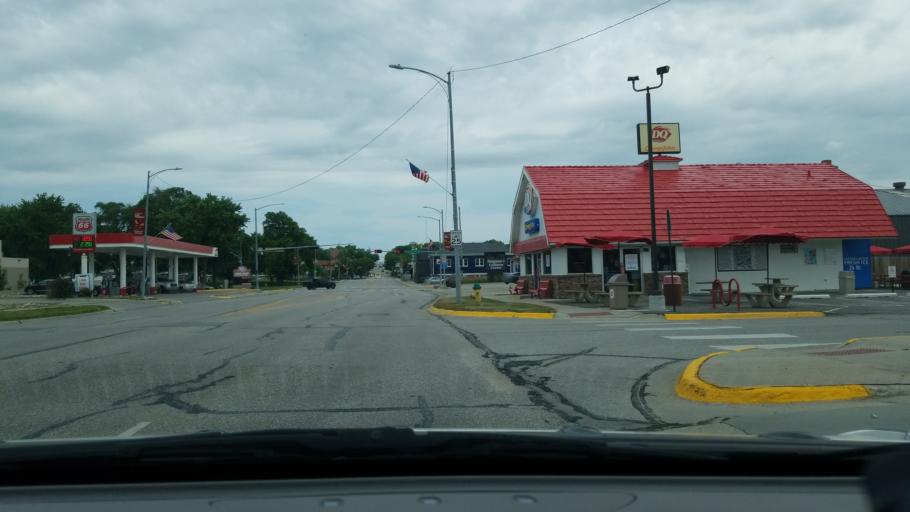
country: US
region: Nebraska
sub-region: Sarpy County
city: Papillion
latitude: 41.1534
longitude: -96.0429
